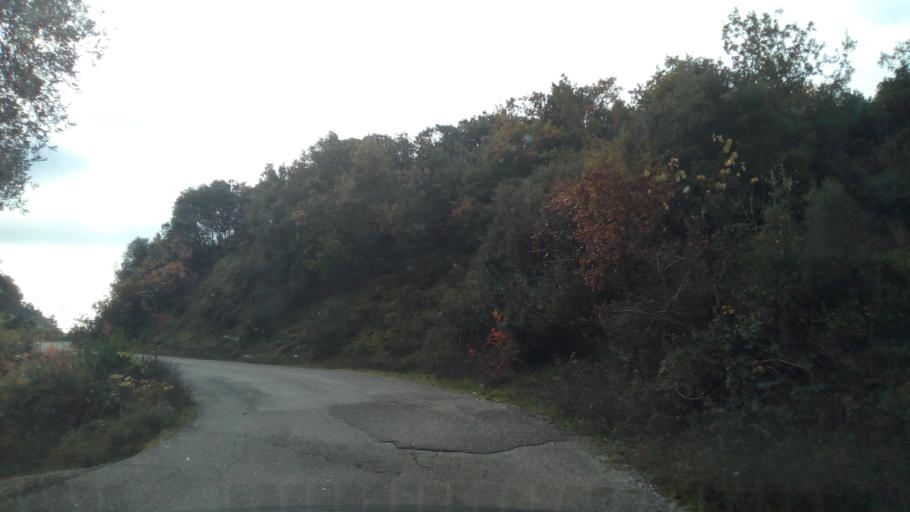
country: GR
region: West Greece
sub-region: Nomos Aitolias kai Akarnanias
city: Nafpaktos
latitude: 38.5244
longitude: 21.9777
